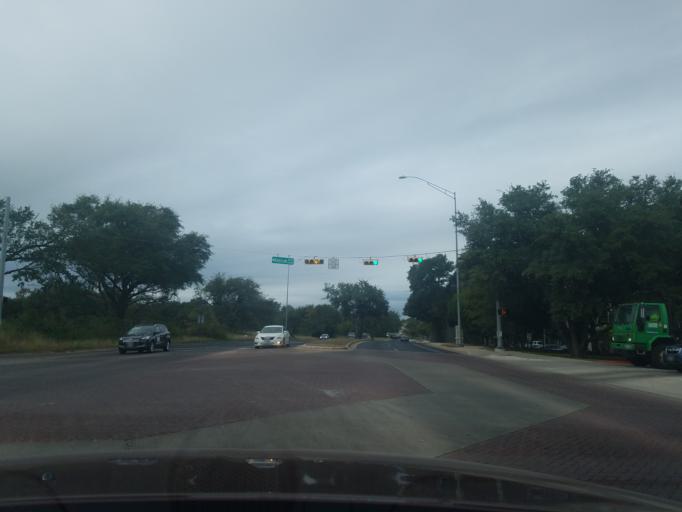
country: US
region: Texas
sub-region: Williamson County
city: Anderson Mill
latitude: 30.4754
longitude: -97.8107
